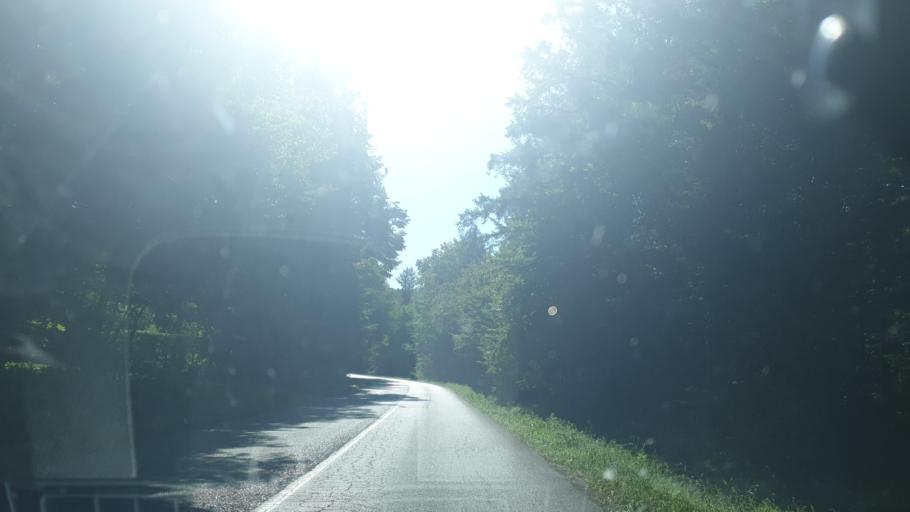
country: RS
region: Central Serbia
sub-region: Kolubarski Okrug
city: Lajkovac
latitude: 44.3158
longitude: 20.1820
